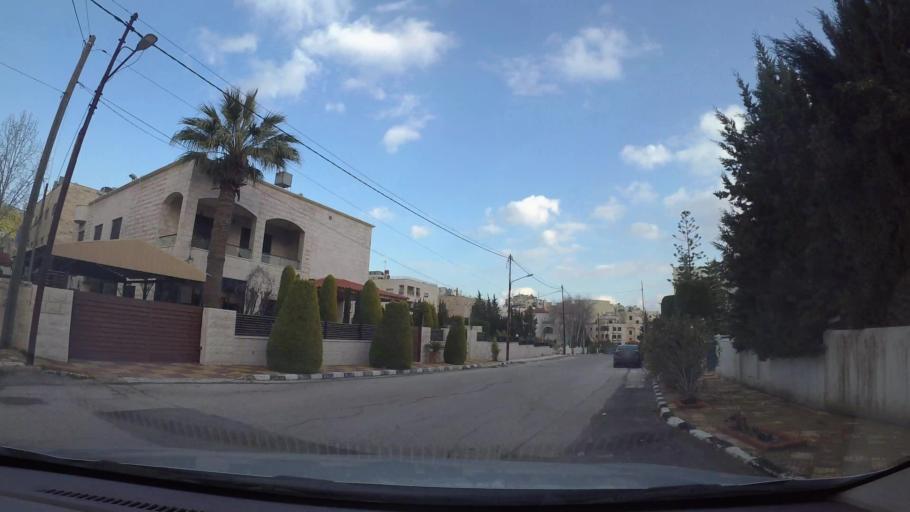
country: JO
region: Amman
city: Al Jubayhah
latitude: 31.9814
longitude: 35.8626
